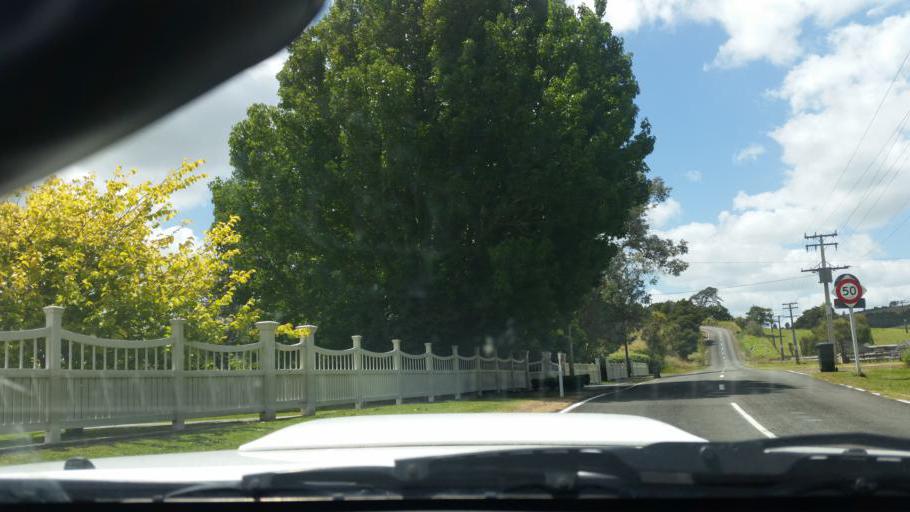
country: NZ
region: Northland
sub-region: Whangarei
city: Ruakaka
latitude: -36.0988
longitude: 174.2320
